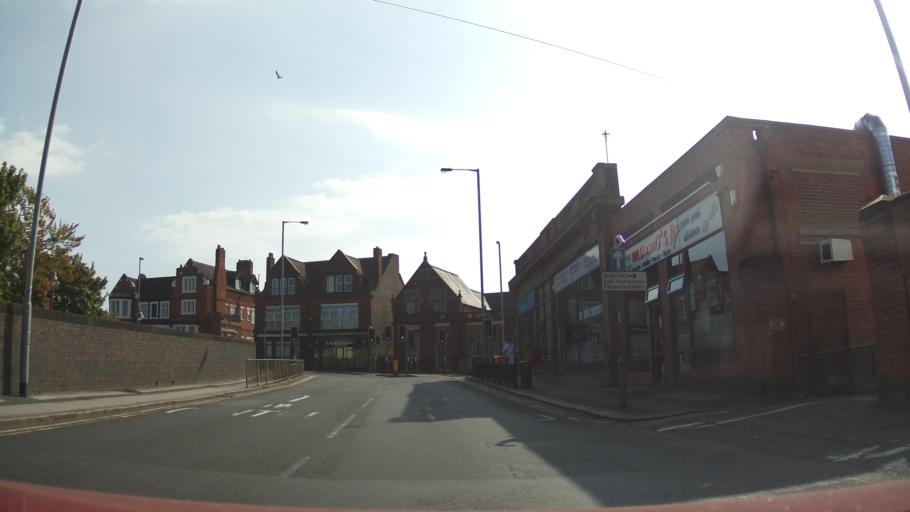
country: GB
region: England
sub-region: Staffordshire
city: Burton upon Trent
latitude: 52.8076
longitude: -1.6430
